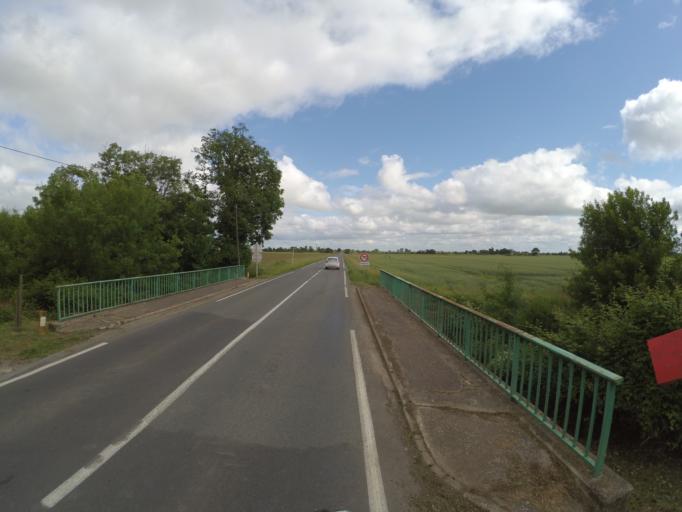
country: FR
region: Aquitaine
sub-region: Departement de la Gironde
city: Ludon-Medoc
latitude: 44.9803
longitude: -0.5636
